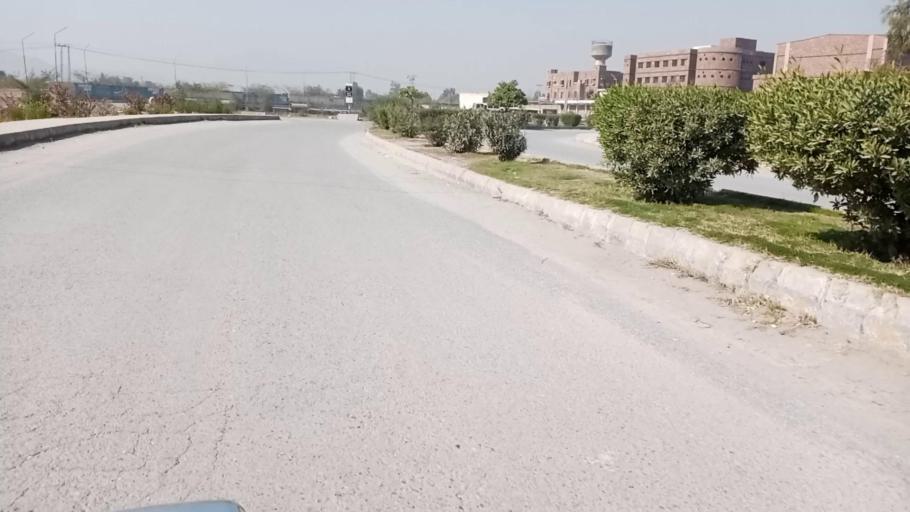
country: PK
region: Khyber Pakhtunkhwa
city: Peshawar
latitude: 33.9565
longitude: 71.4186
